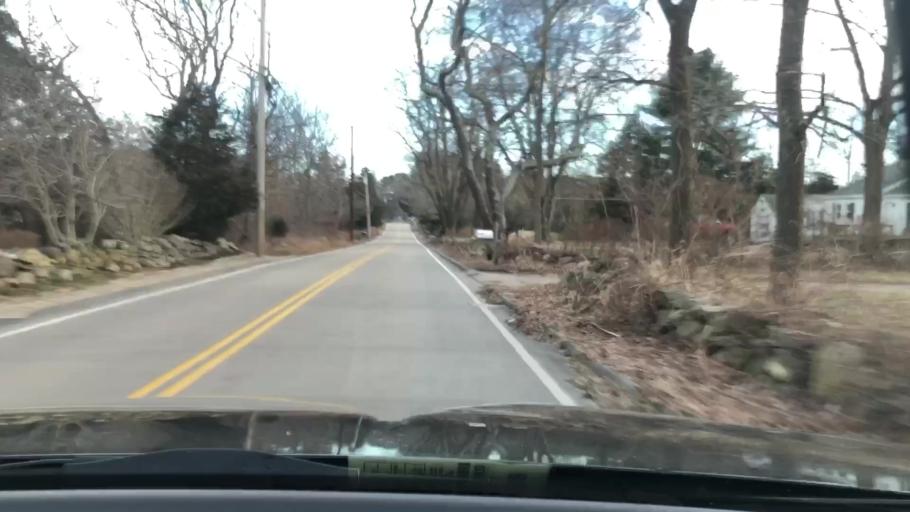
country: US
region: Massachusetts
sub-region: Worcester County
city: Blackstone
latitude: 42.0465
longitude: -71.5292
